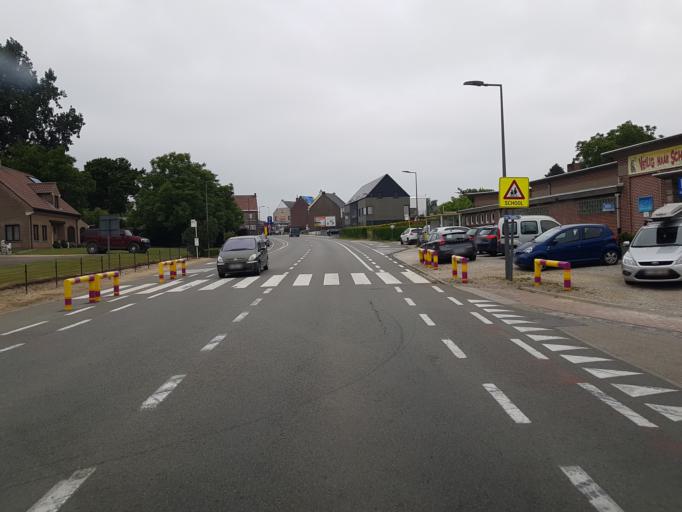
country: BE
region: Flanders
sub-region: Provincie Oost-Vlaanderen
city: Haaltert
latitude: 50.8534
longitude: 3.9595
